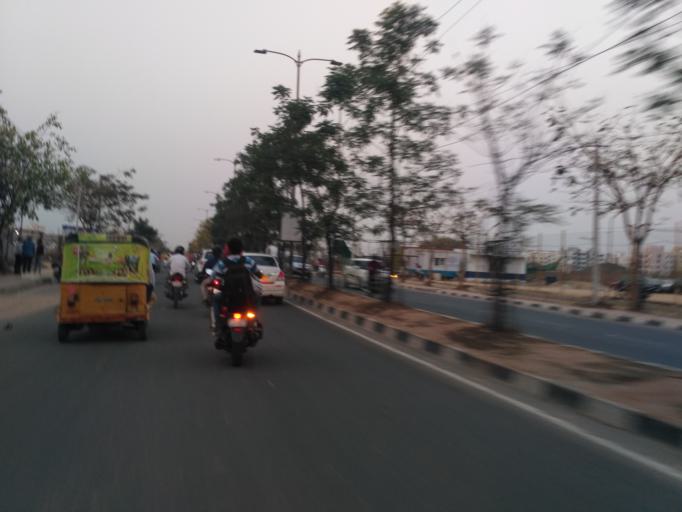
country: IN
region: Telangana
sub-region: Rangareddi
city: Kukatpalli
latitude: 17.4438
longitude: 78.3938
